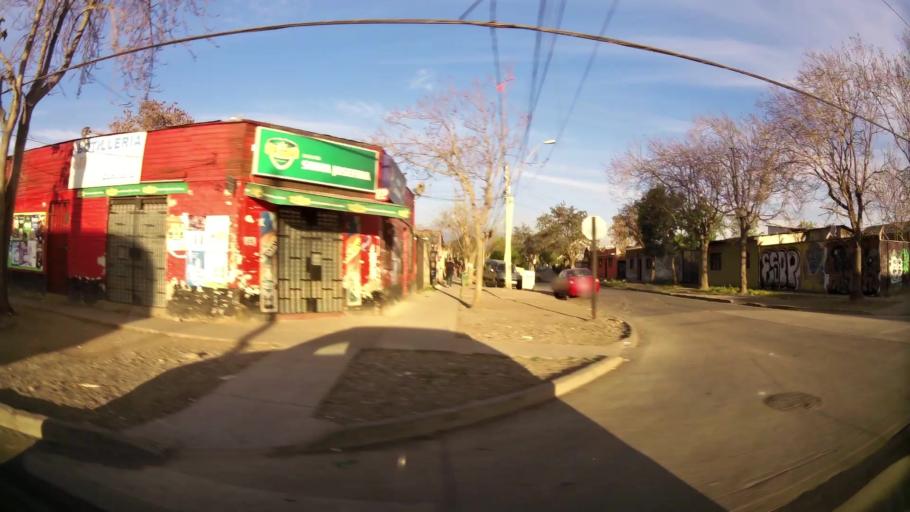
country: CL
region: Santiago Metropolitan
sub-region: Provincia de Santiago
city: Lo Prado
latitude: -33.4276
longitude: -70.7194
